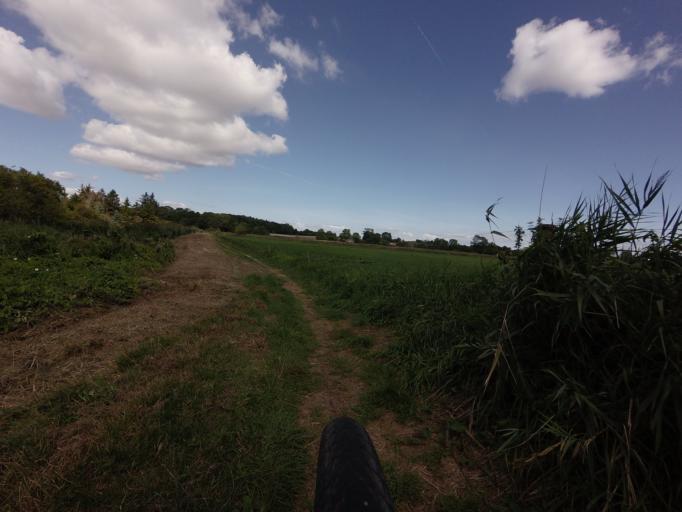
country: DK
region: Zealand
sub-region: Vordingborg Kommune
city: Stege
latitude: 54.9638
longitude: 12.4188
